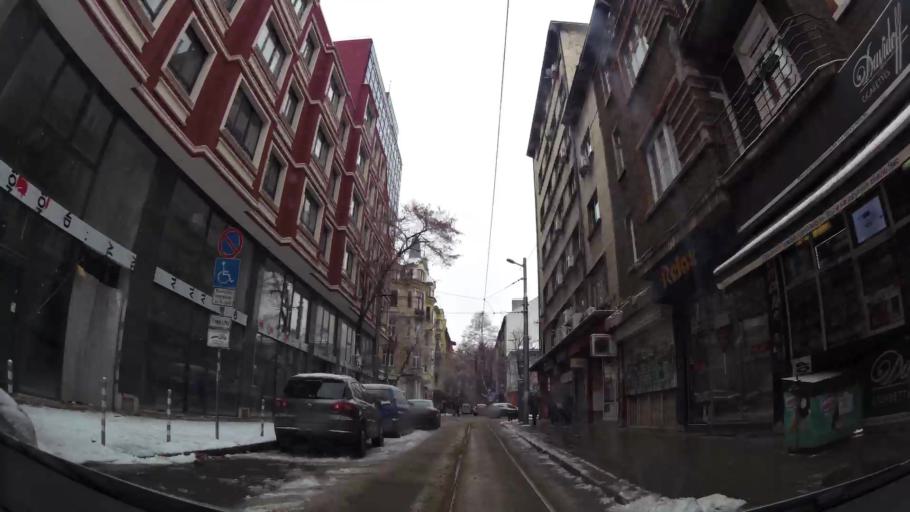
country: BG
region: Sofia-Capital
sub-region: Stolichna Obshtina
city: Sofia
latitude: 42.6955
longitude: 23.3185
